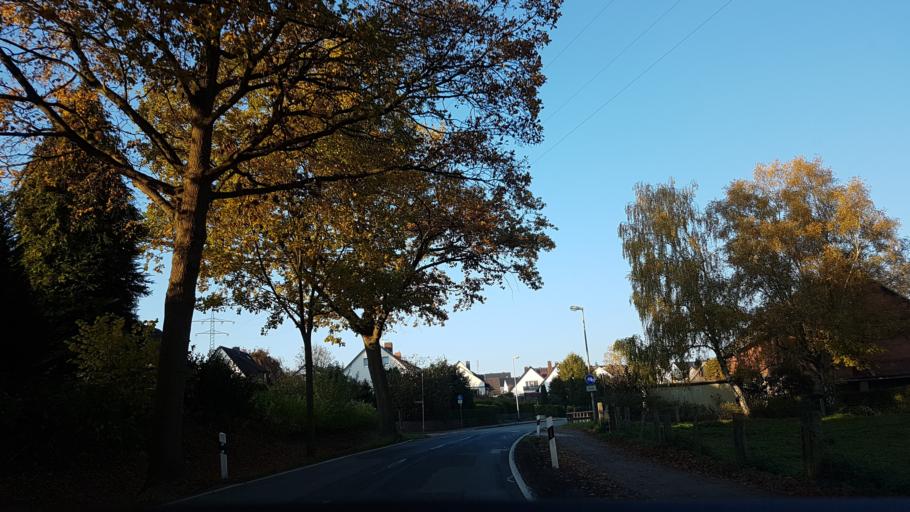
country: DE
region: Lower Saxony
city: Hameln
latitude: 52.1371
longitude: 9.3775
